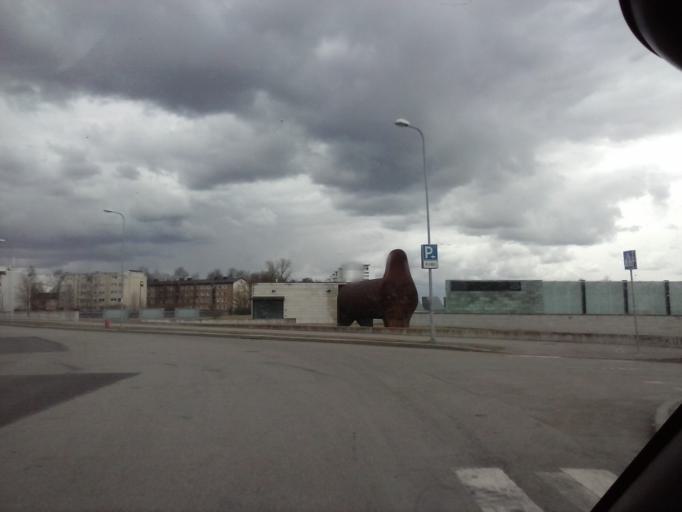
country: EE
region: Harju
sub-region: Tallinna linn
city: Tallinn
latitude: 59.4366
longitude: 24.7990
